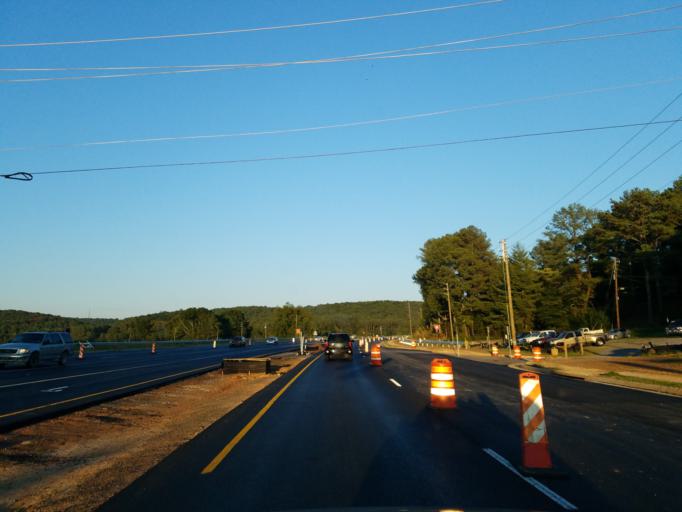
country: US
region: Georgia
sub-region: Bartow County
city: Cartersville
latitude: 34.2063
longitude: -84.7806
